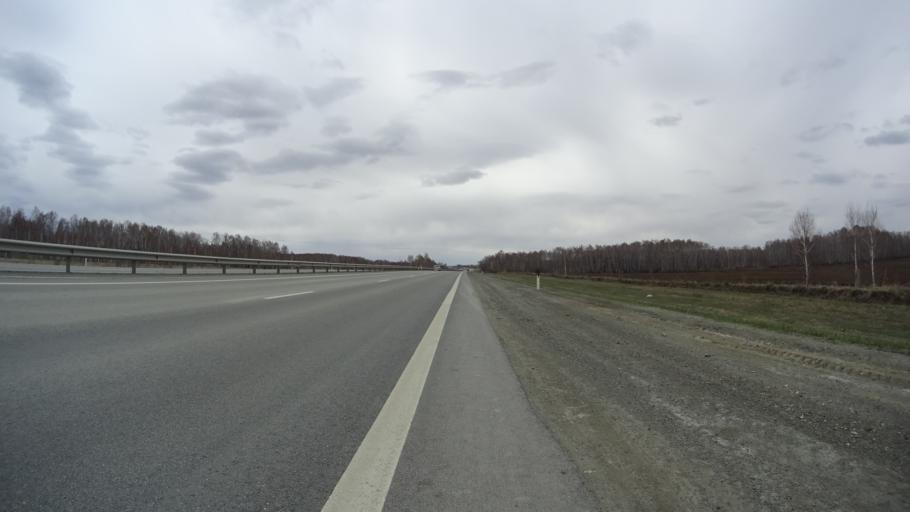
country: RU
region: Chelyabinsk
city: Yemanzhelinka
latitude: 54.8311
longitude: 61.3116
